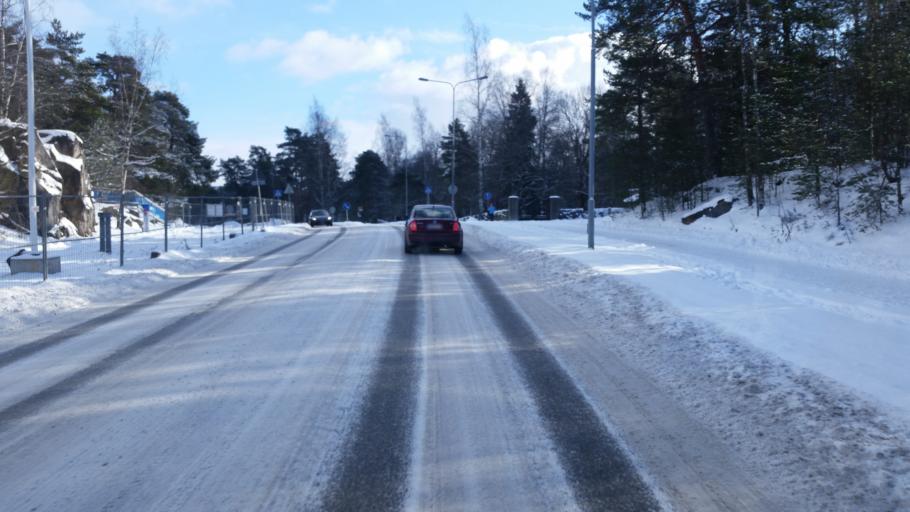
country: FI
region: Varsinais-Suomi
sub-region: Turku
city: Turku
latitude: 60.4359
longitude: 22.3047
